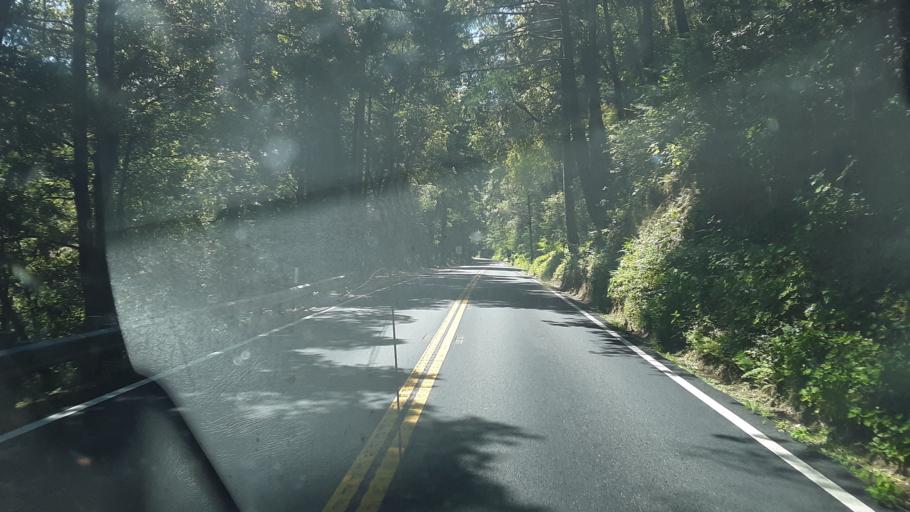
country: US
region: California
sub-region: Del Norte County
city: Bertsch-Oceanview
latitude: 41.8344
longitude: -124.0363
